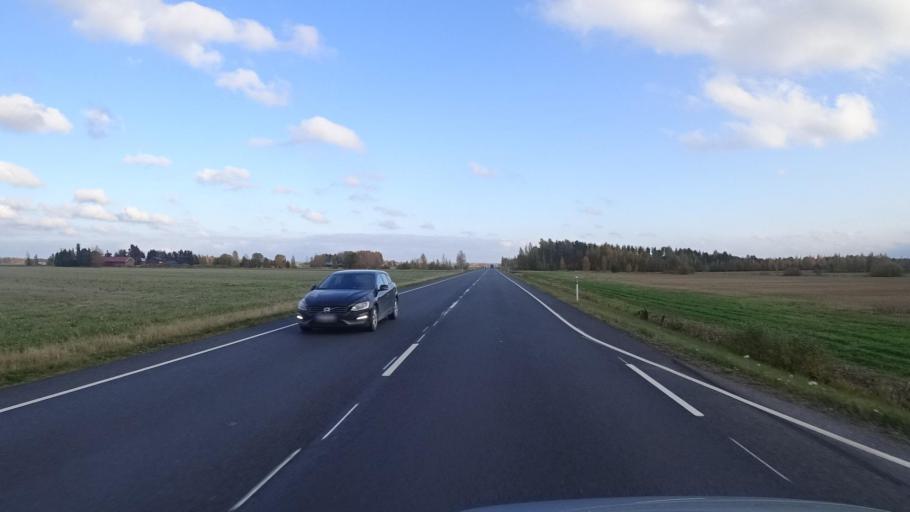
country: FI
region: Satakunta
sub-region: Rauma
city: Koeylioe
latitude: 61.0747
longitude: 22.2958
